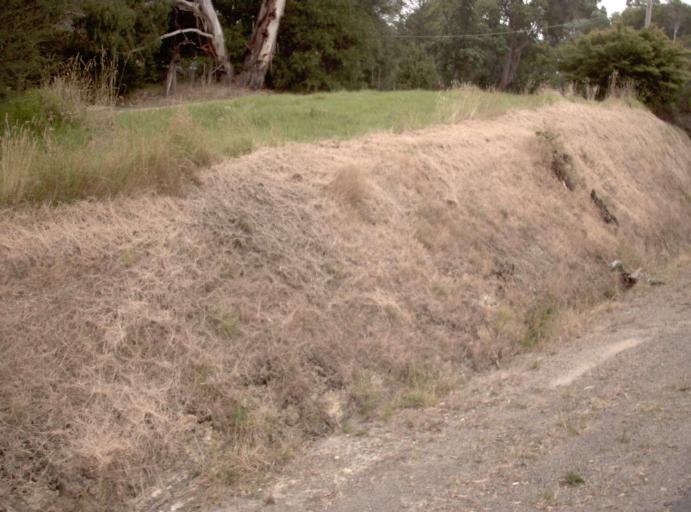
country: AU
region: Victoria
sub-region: Yarra Ranges
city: Badger Creek
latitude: -37.6844
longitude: 145.5349
